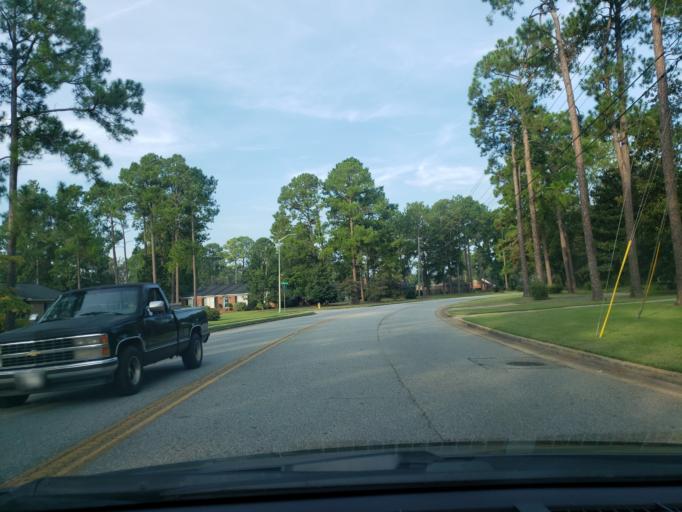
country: US
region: Georgia
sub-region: Dougherty County
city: Albany
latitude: 31.5999
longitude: -84.2152
